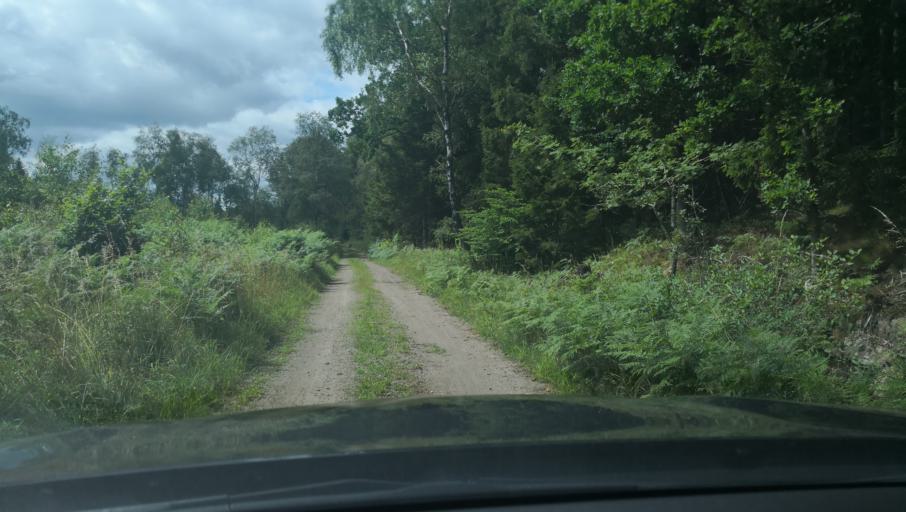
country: SE
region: Skane
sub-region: Simrishamns Kommun
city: Kivik
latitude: 55.6209
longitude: 14.1127
